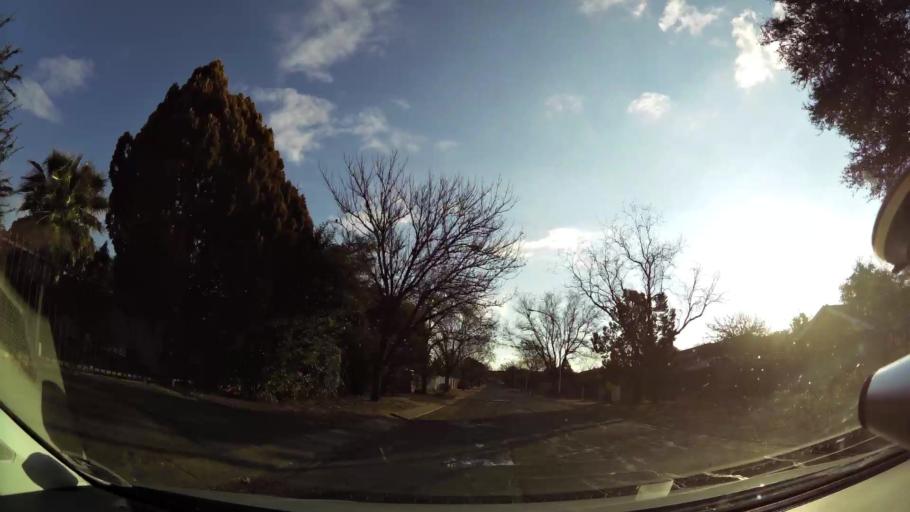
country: ZA
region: Orange Free State
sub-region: Mangaung Metropolitan Municipality
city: Bloemfontein
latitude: -29.1490
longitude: 26.1828
